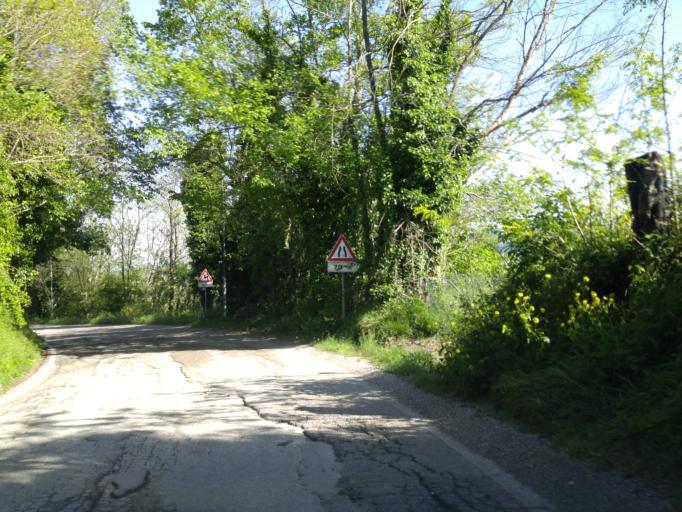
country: IT
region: The Marches
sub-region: Provincia di Pesaro e Urbino
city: Monteciccardo
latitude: 43.8283
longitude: 12.8166
